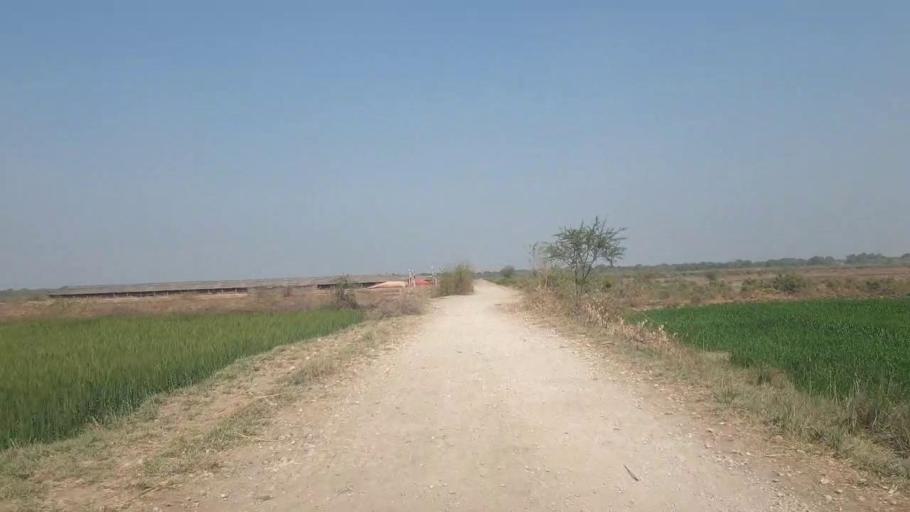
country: PK
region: Sindh
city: Tando Allahyar
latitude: 25.4390
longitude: 68.8359
